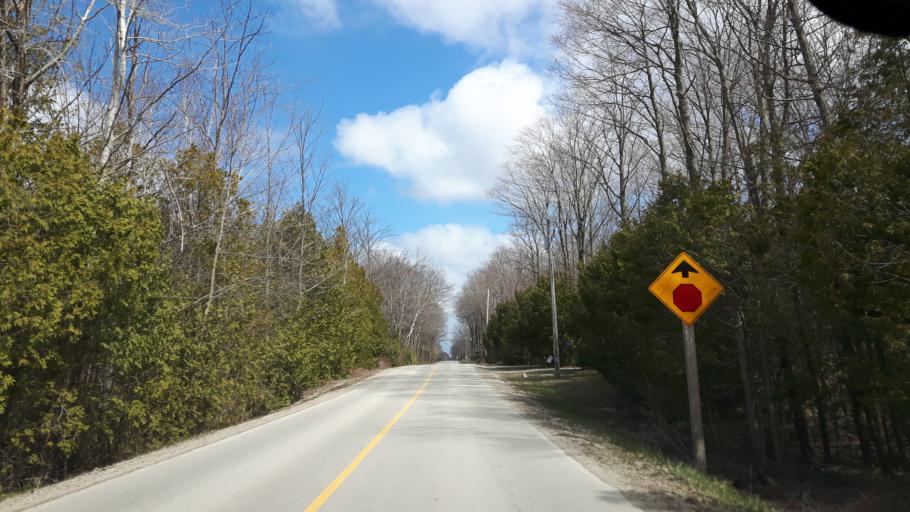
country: CA
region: Ontario
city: Bluewater
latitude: 43.5840
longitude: -81.6848
